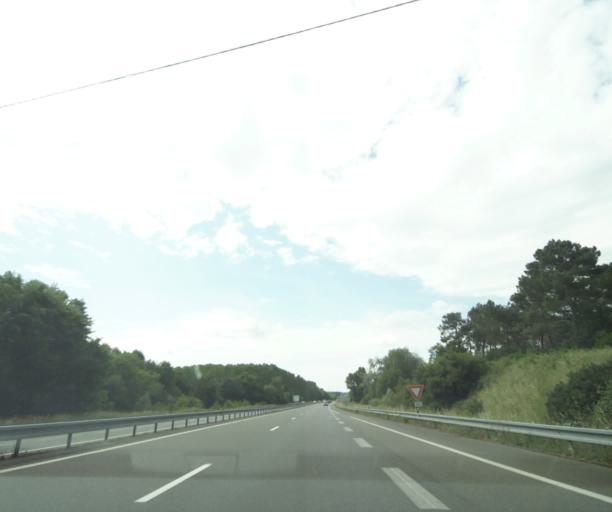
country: FR
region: Pays de la Loire
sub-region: Departement de Maine-et-Loire
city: Brion
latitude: 47.4215
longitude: -0.1381
